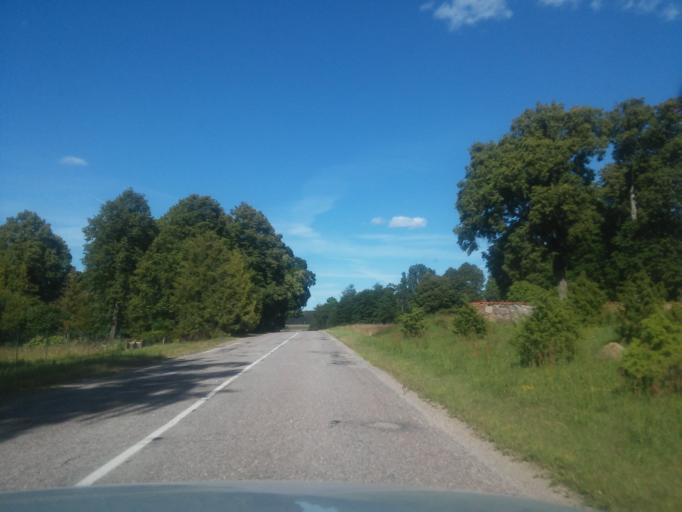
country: LV
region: Skrunda
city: Skrunda
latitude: 56.6252
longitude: 21.9817
